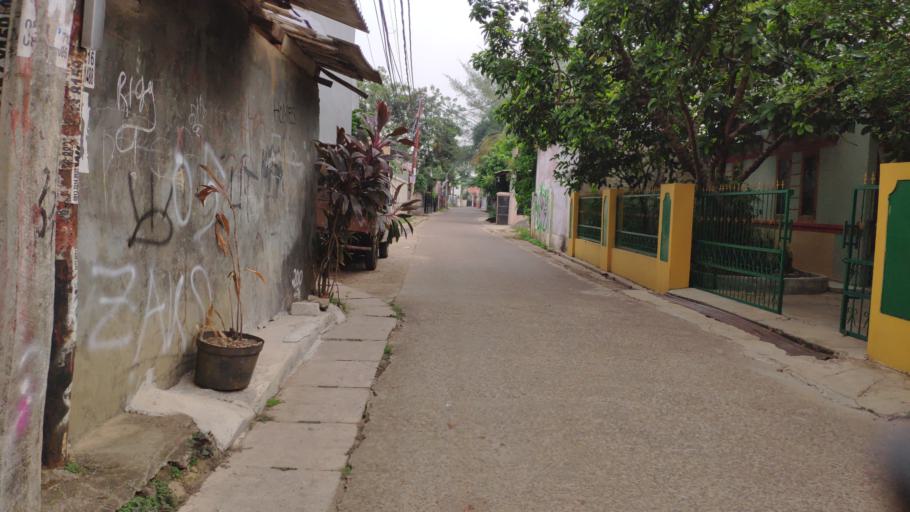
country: ID
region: West Java
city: Depok
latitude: -6.3762
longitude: 106.7986
